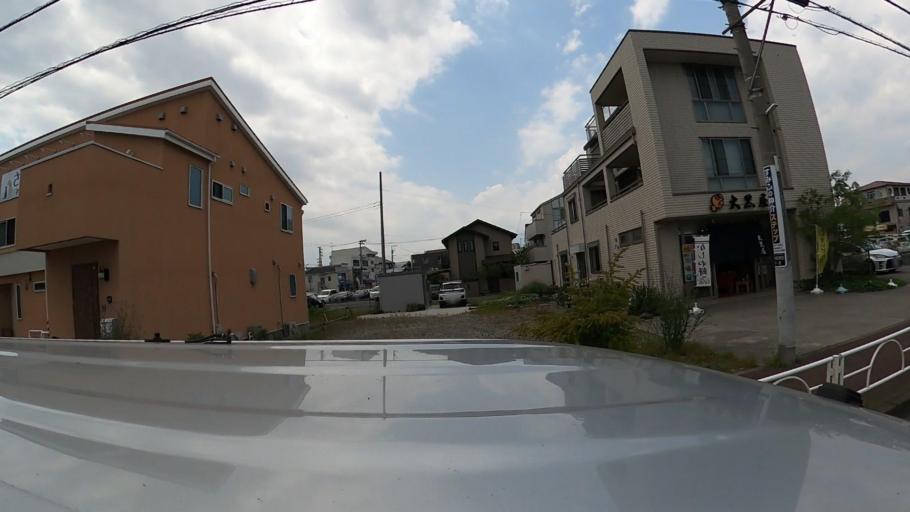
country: JP
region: Kanagawa
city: Chigasaki
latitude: 35.3675
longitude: 139.3892
